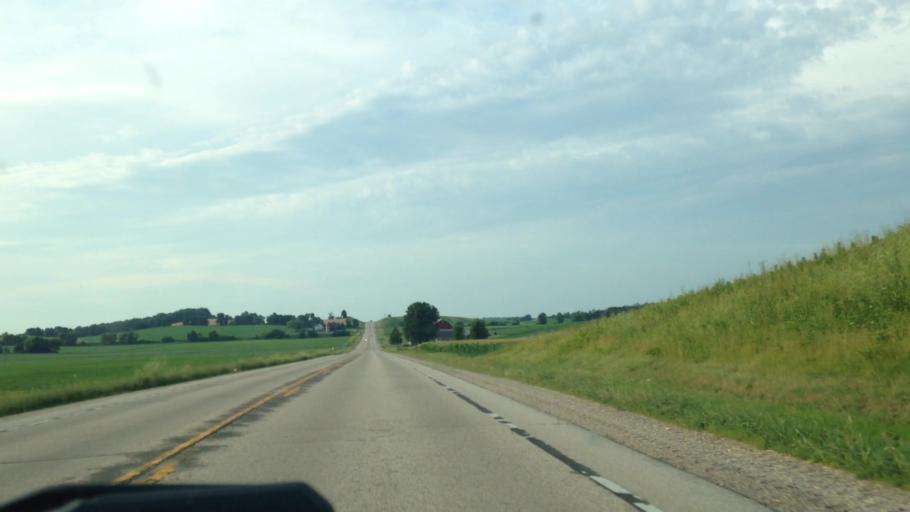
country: US
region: Wisconsin
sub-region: Dodge County
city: Theresa
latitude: 43.4678
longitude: -88.4501
